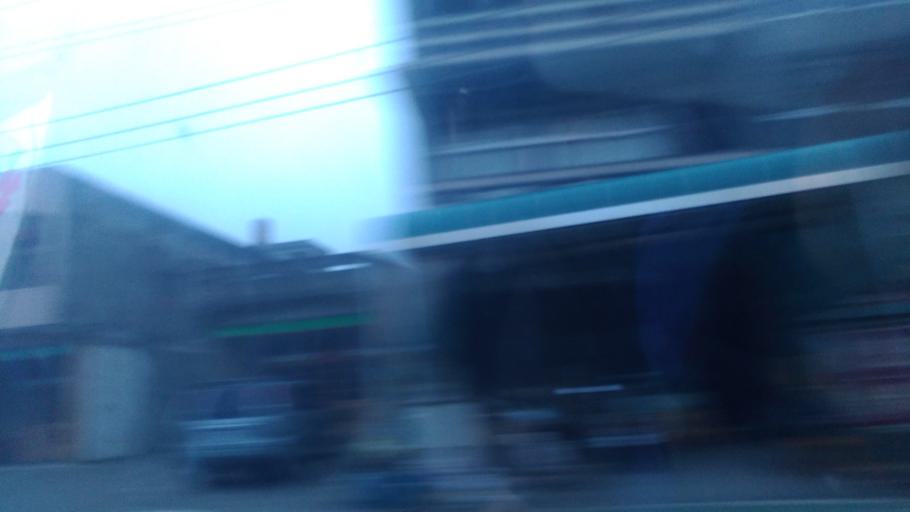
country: TW
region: Taiwan
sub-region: Miaoli
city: Miaoli
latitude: 24.5610
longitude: 120.7078
